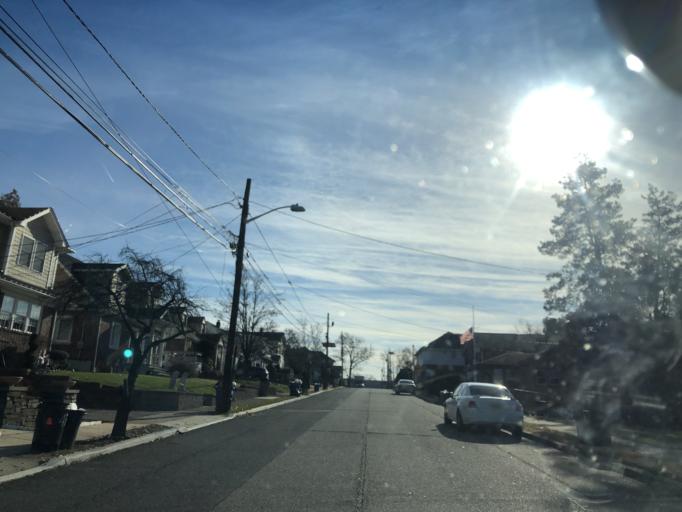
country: US
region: New Jersey
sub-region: Bergen County
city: Fair Lawn
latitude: 40.9213
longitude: -74.1286
